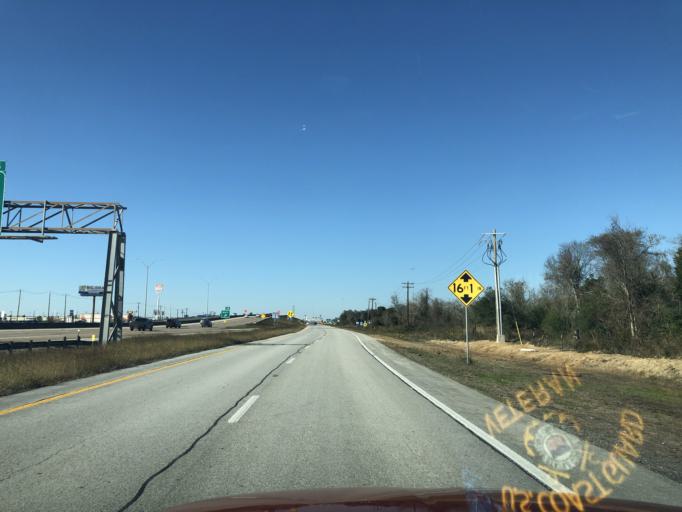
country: US
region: Texas
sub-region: Galveston County
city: Hitchcock
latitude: 29.3994
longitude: -95.0293
